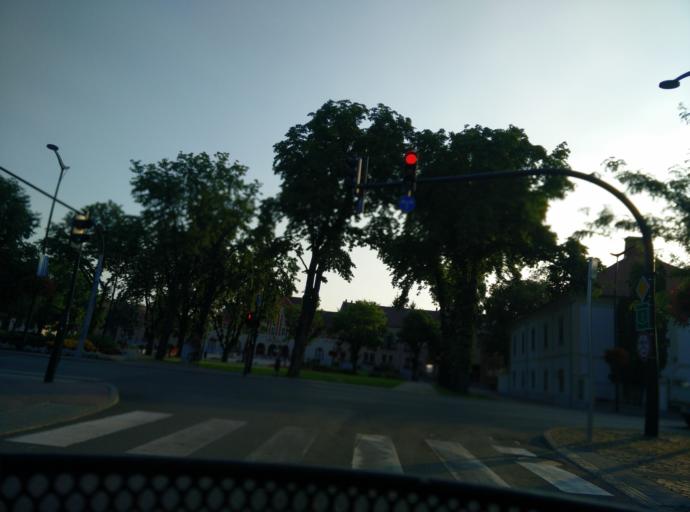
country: HU
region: Heves
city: Hatvan
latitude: 47.6668
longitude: 19.6841
